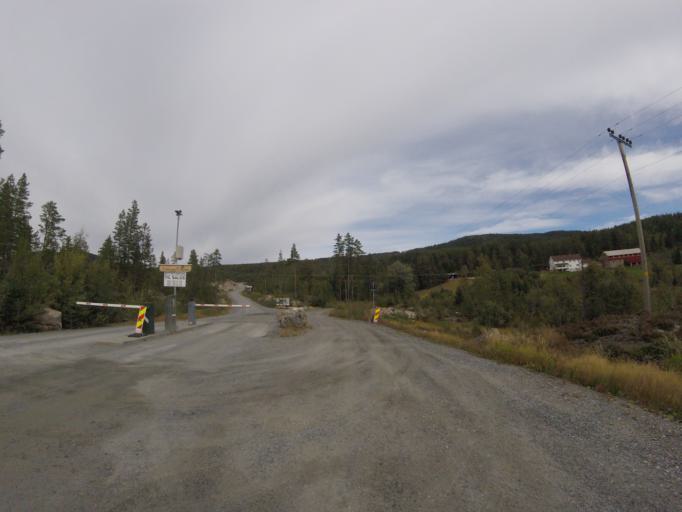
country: NO
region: Telemark
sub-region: Notodden
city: Notodden
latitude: 59.7337
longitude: 9.3873
